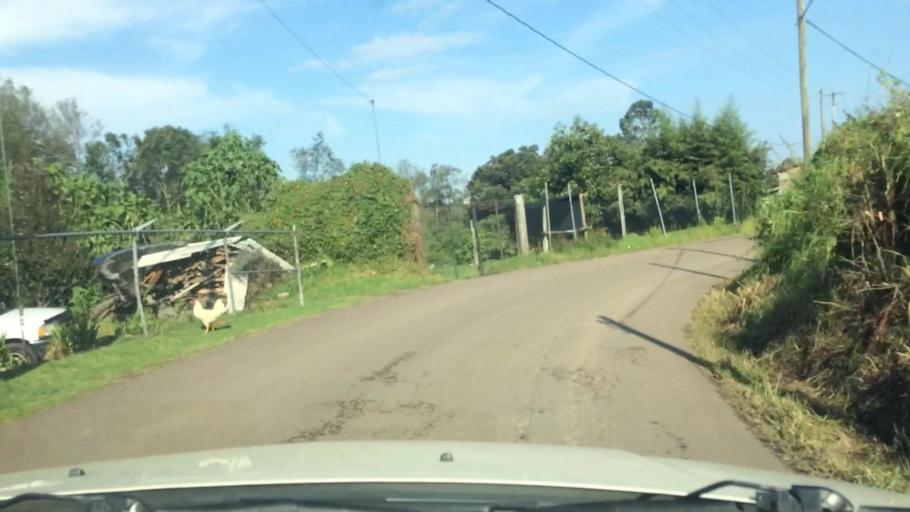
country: MX
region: Mexico
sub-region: Valle de Bravo
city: Cuadrilla de Dolores
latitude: 19.1511
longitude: -100.0576
